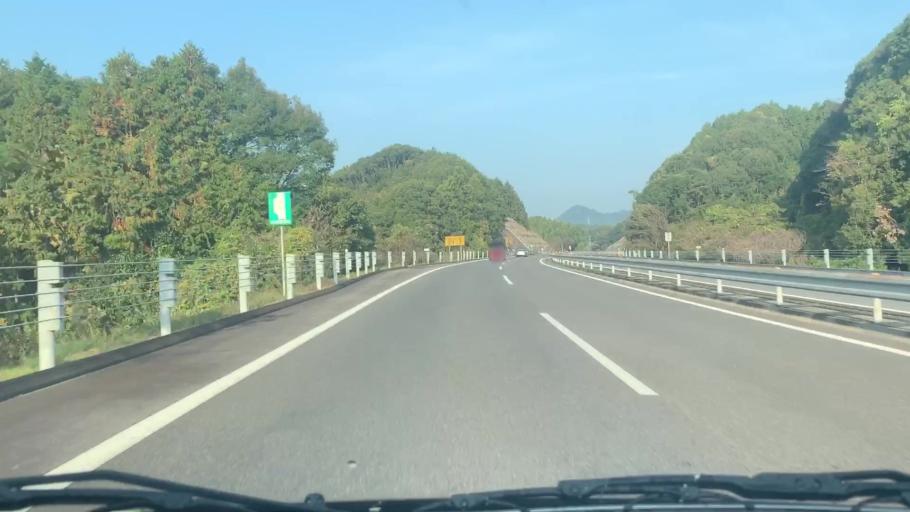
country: JP
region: Saga Prefecture
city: Ureshinomachi-shimojuku
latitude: 33.1499
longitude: 129.9368
